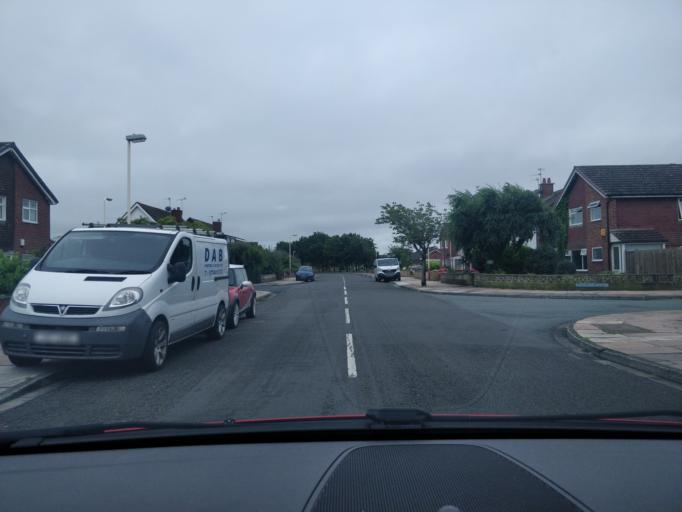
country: GB
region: England
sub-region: Lancashire
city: Banks
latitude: 53.6757
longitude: -2.9592
